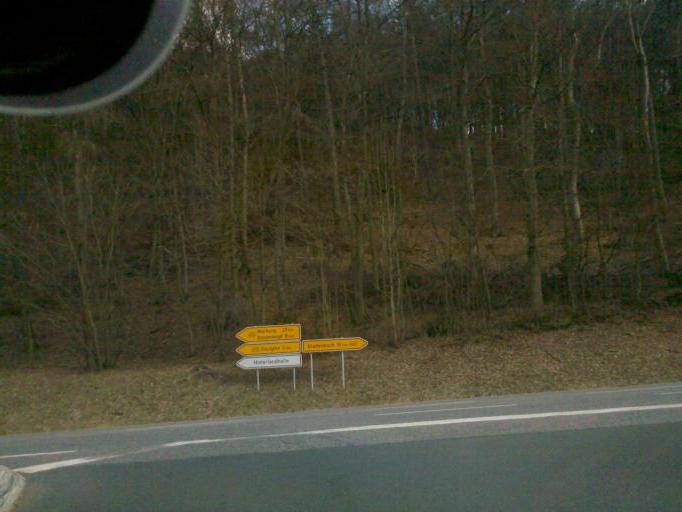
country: DE
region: Hesse
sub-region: Regierungsbezirk Giessen
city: Biedenkopf
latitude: 50.8467
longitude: 8.5446
